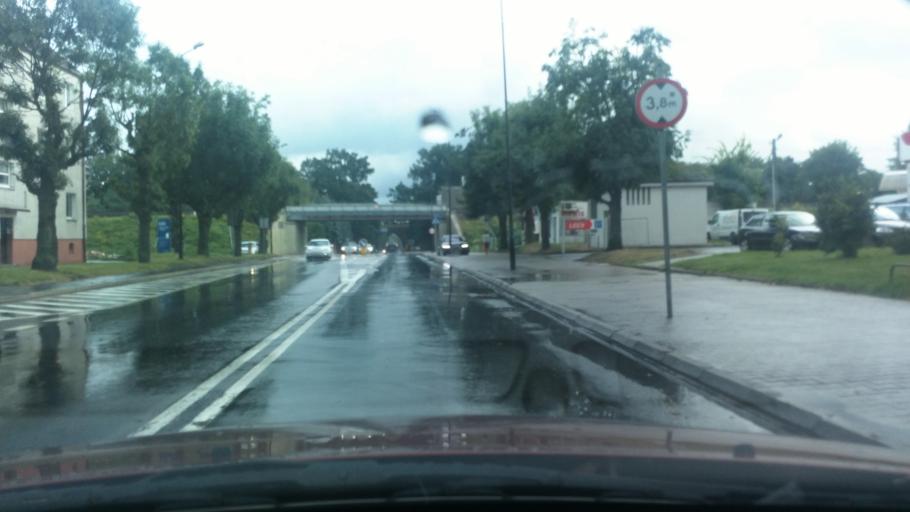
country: PL
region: Lower Silesian Voivodeship
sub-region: Powiat zgorzelecki
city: Zgorzelec
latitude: 51.1430
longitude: 15.0104
